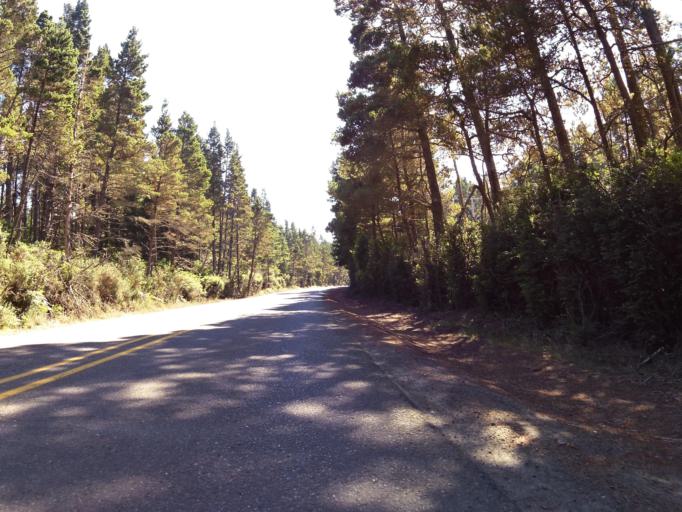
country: US
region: Oregon
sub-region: Coos County
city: Bandon
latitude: 43.1865
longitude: -124.3678
